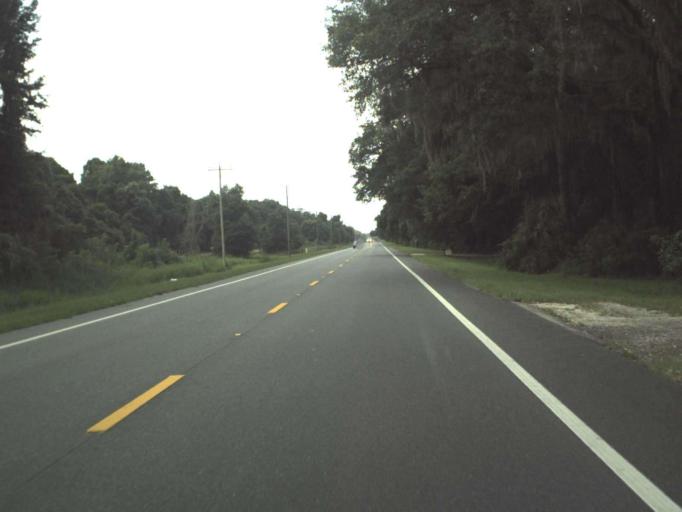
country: US
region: Florida
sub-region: Sumter County
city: Bushnell
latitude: 28.6009
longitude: -82.1430
